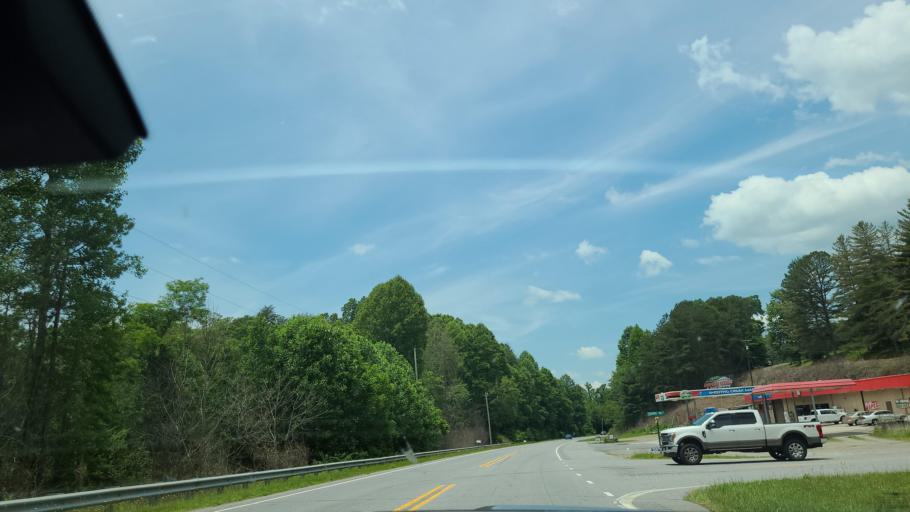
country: US
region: Georgia
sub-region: Towns County
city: Hiawassee
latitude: 35.0224
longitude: -83.6936
